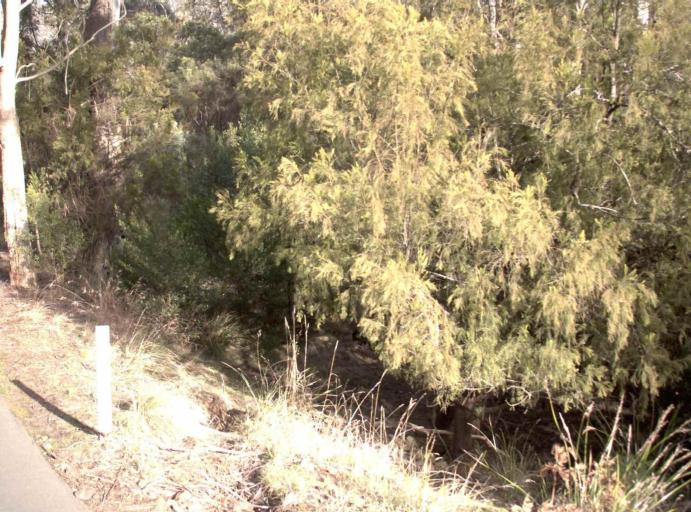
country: AU
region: Tasmania
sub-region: Launceston
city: Summerhill
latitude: -41.4573
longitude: 147.1189
